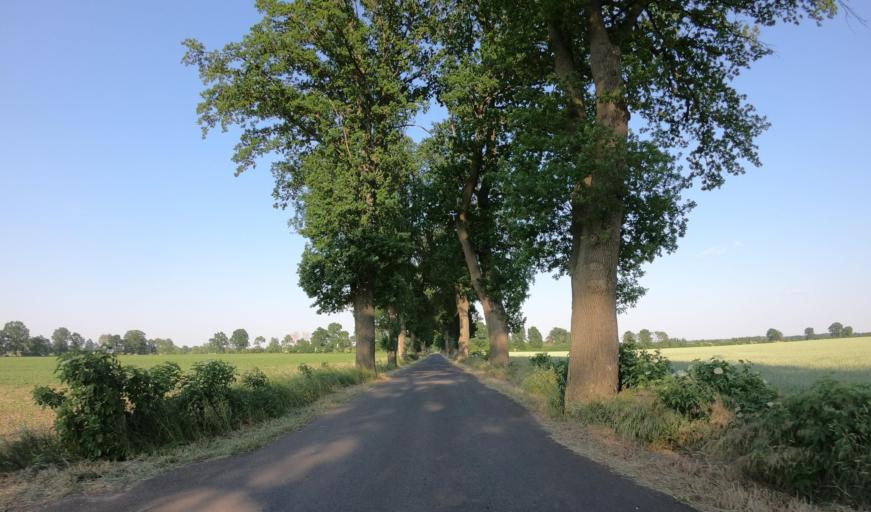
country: PL
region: West Pomeranian Voivodeship
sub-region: Powiat lobeski
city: Radowo Male
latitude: 53.6368
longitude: 15.3902
